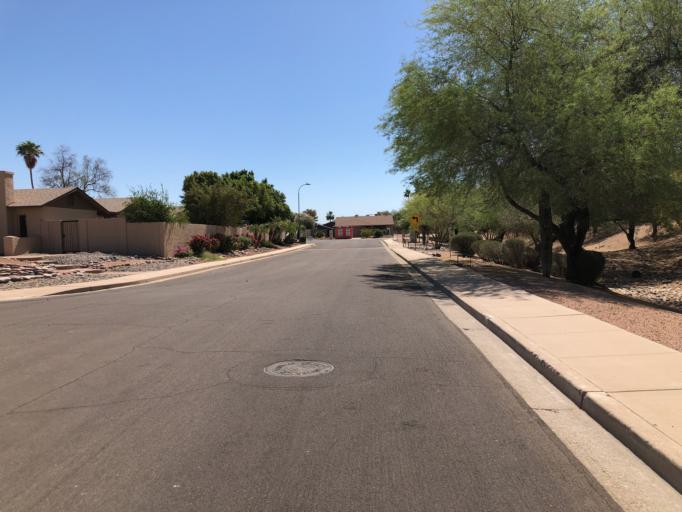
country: US
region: Arizona
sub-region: Maricopa County
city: Tempe
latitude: 33.4554
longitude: -111.8979
